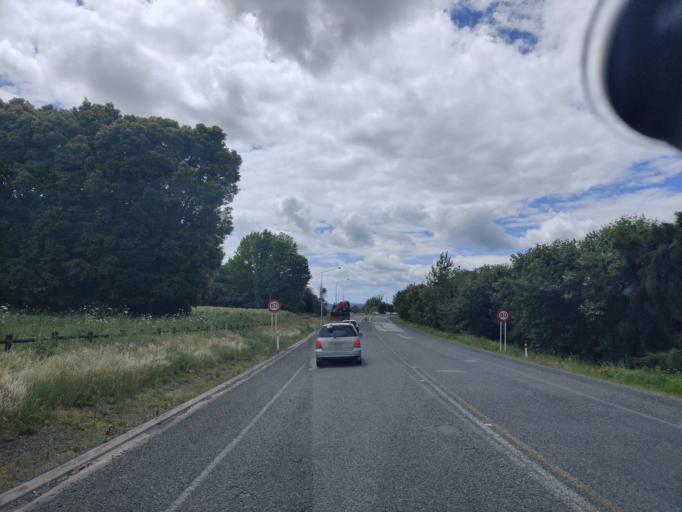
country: NZ
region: Northland
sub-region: Far North District
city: Kerikeri
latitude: -35.2555
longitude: 173.9329
